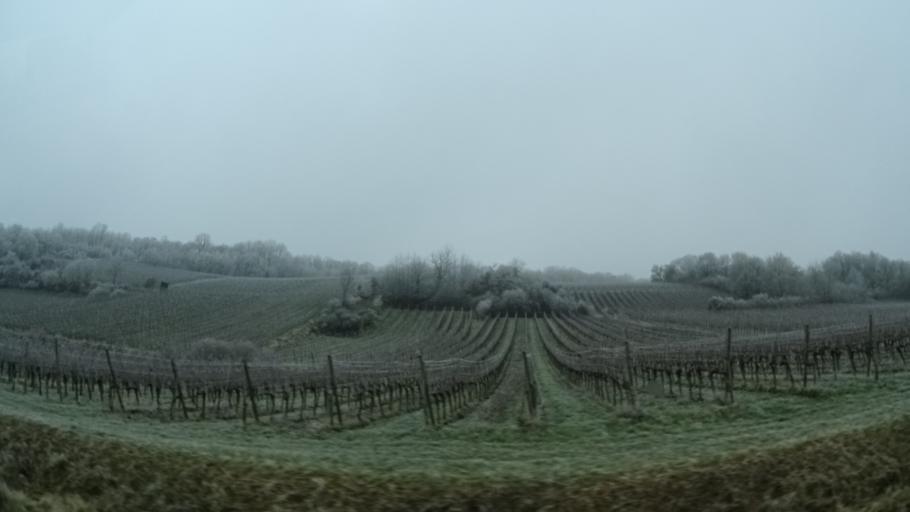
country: DE
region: Bavaria
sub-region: Regierungsbezirk Unterfranken
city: Marktsteft
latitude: 49.6911
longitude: 10.1265
